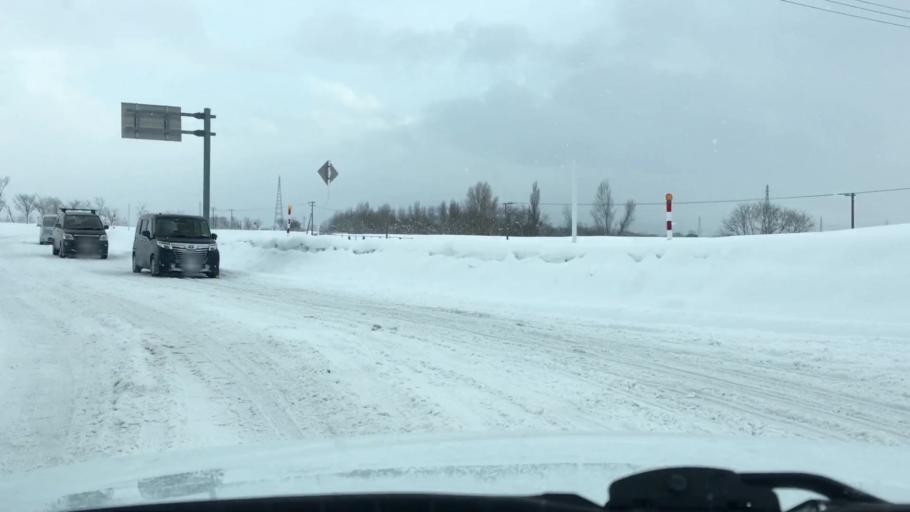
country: JP
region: Aomori
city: Hirosaki
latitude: 40.6524
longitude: 140.4727
